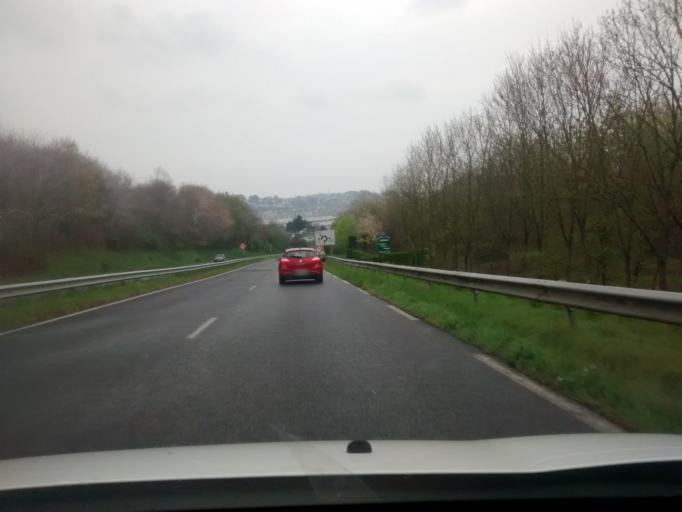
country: FR
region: Brittany
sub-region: Departement des Cotes-d'Armor
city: Saint-Quay-Perros
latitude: 48.7933
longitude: -3.4417
